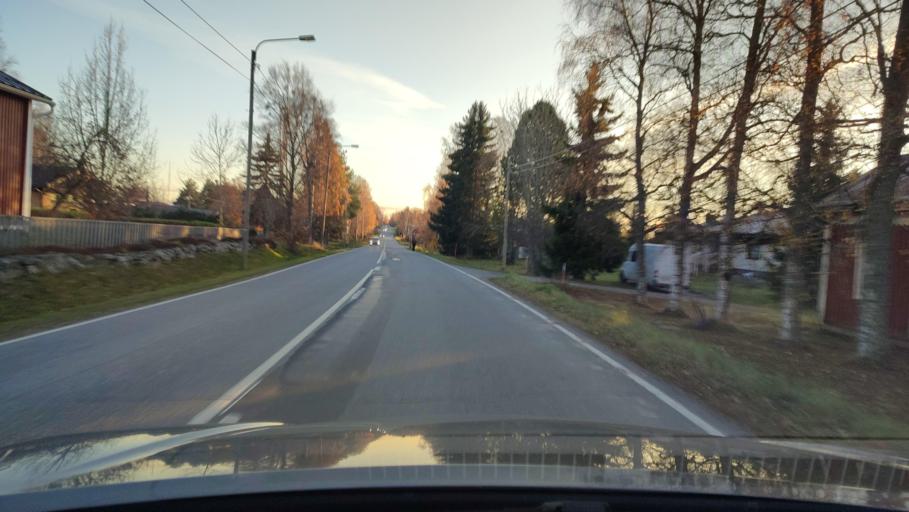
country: FI
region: Ostrobothnia
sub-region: Sydosterbotten
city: Naerpes
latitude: 62.4948
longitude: 21.3435
